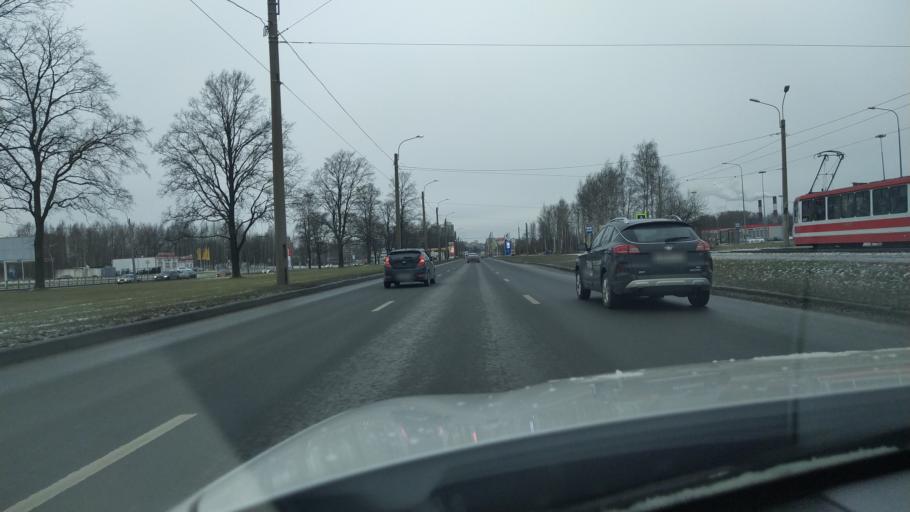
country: RU
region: St.-Petersburg
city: Grazhdanka
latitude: 60.0171
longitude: 30.4329
